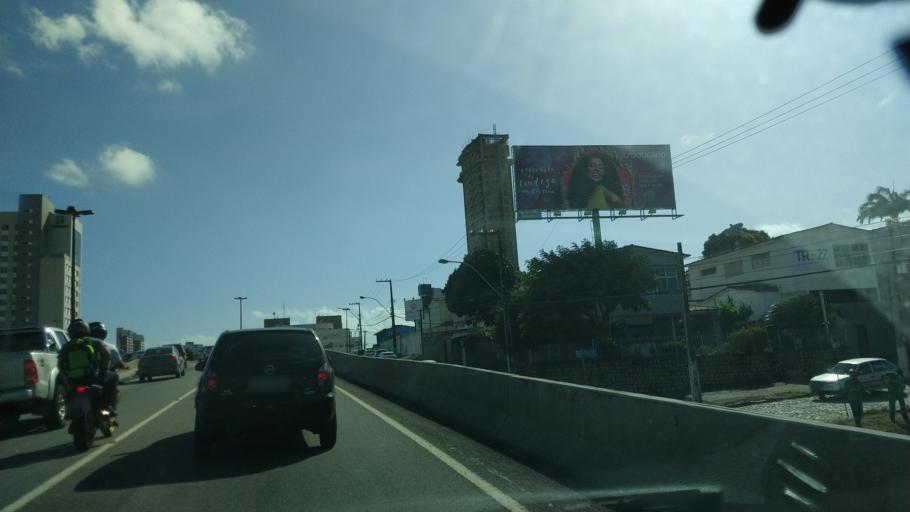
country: BR
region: Rio Grande do Norte
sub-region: Natal
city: Natal
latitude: -5.8276
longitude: -35.2102
